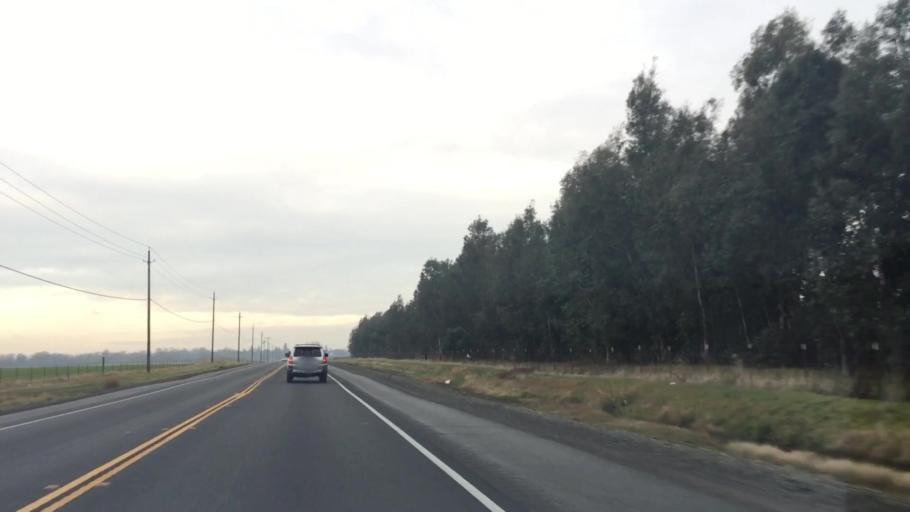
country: US
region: California
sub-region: Butte County
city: Palermo
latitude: 39.4105
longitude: -121.6048
